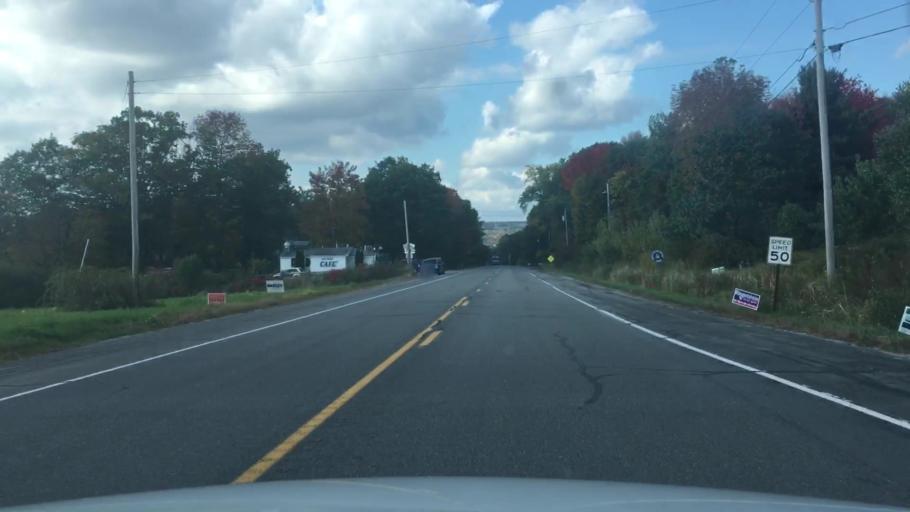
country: US
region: Maine
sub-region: Knox County
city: Union
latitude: 44.2133
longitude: -69.2643
